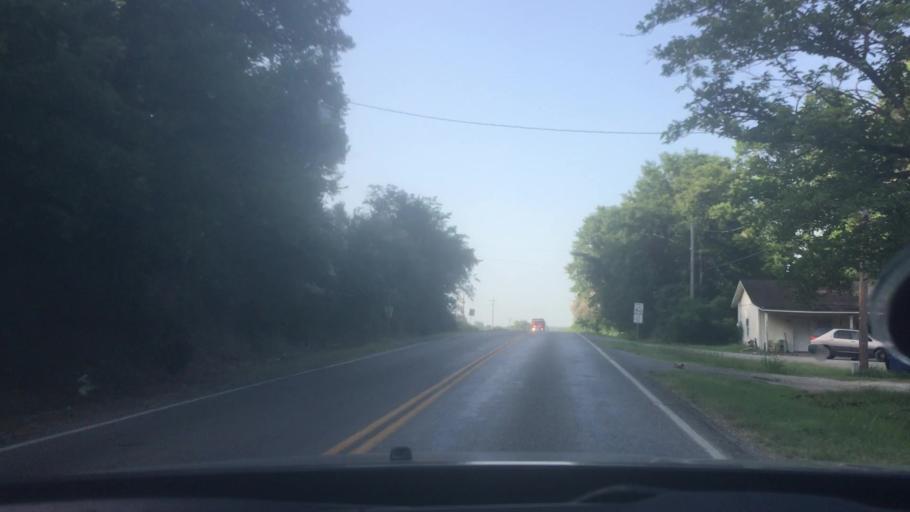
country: US
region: Oklahoma
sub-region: Coal County
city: Coalgate
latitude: 34.3677
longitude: -96.4245
